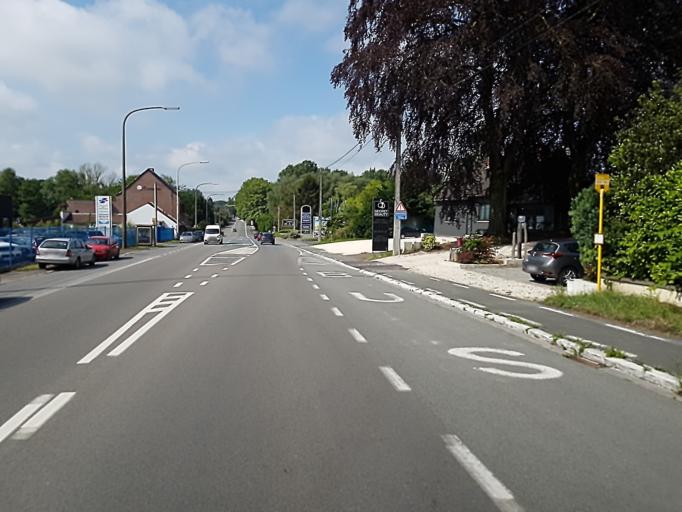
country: BE
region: Wallonia
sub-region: Province du Hainaut
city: Mons
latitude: 50.5093
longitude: 4.0055
